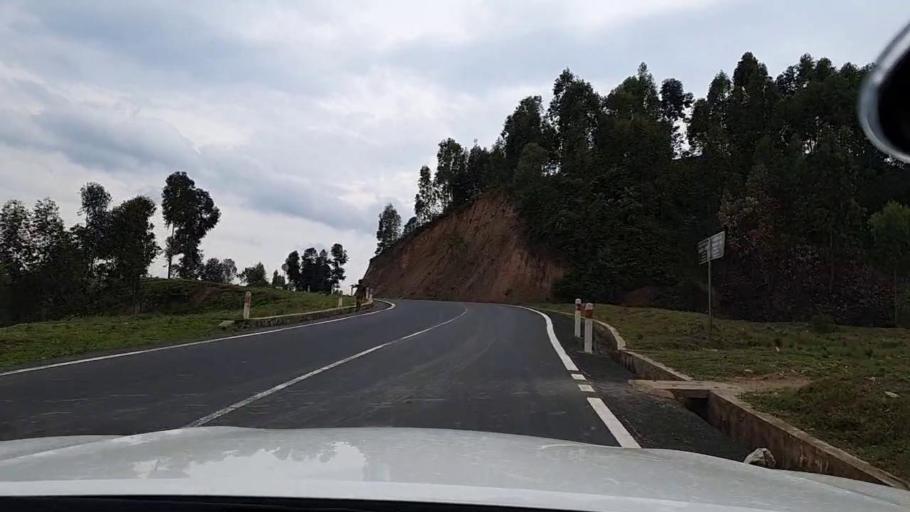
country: RW
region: Western Province
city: Kibuye
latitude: -2.1777
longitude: 29.2885
